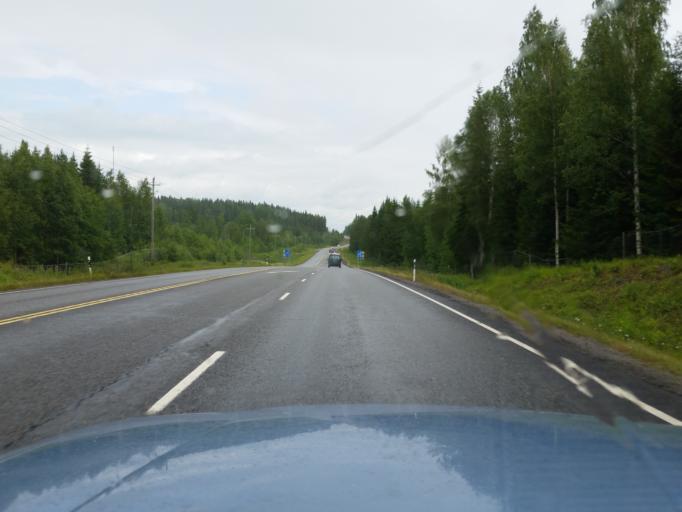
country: FI
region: Southern Savonia
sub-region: Mikkeli
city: Pertunmaa
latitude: 61.4367
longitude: 26.5119
